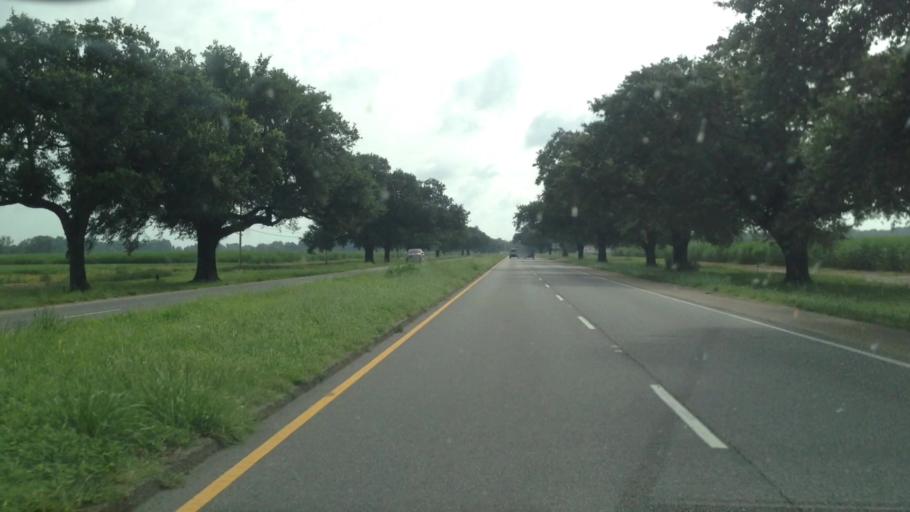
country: US
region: Louisiana
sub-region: West Baton Rouge Parish
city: Port Allen
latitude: 30.4992
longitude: -91.2422
